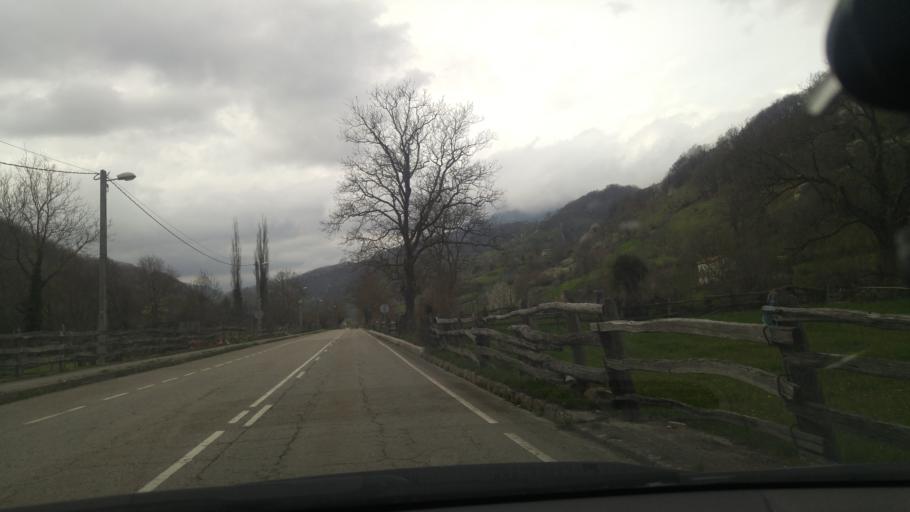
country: ES
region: Asturias
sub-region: Province of Asturias
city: Rio Aller
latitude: 43.1084
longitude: -5.5220
